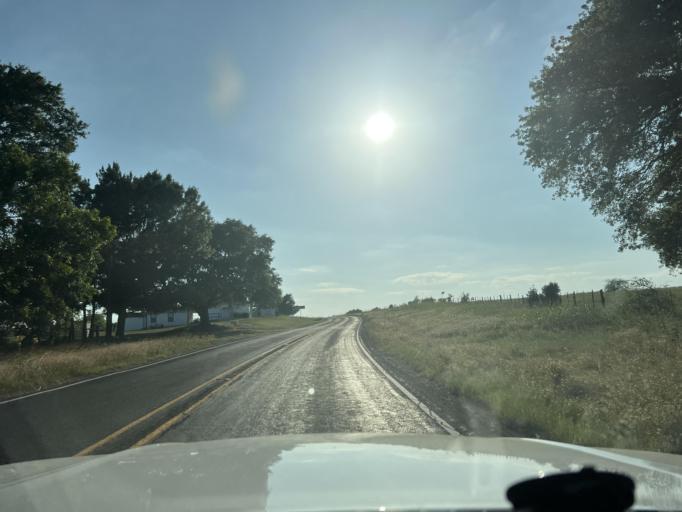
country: US
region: Texas
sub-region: Washington County
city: Brenham
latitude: 30.2406
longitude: -96.2472
